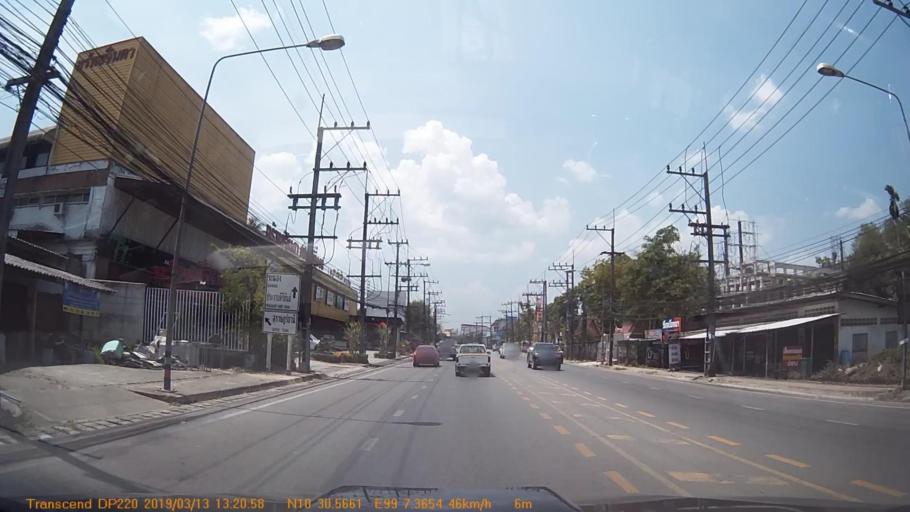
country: TH
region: Chumphon
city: Chumphon
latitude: 10.5086
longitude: 99.1241
